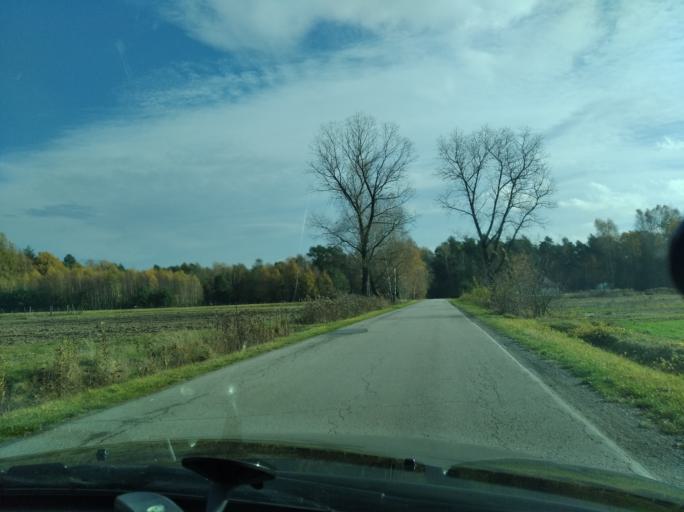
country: PL
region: Subcarpathian Voivodeship
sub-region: Powiat ropczycko-sedziszowski
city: Sedziszow Malopolski
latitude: 50.1224
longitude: 21.7120
